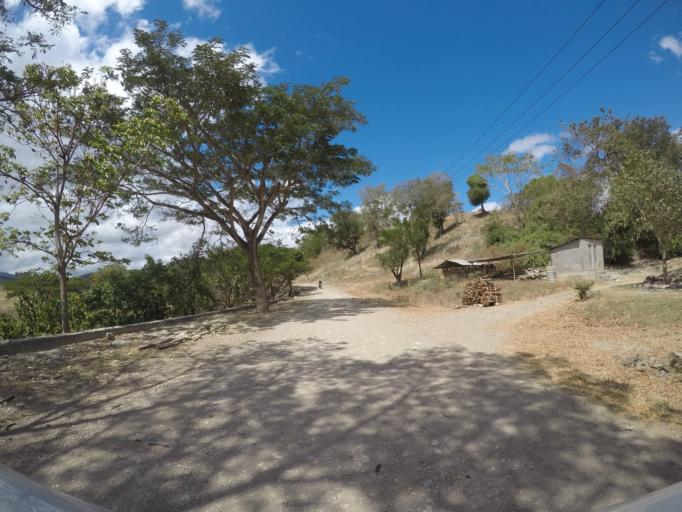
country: TL
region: Lautem
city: Lospalos
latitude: -8.4864
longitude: 126.8193
